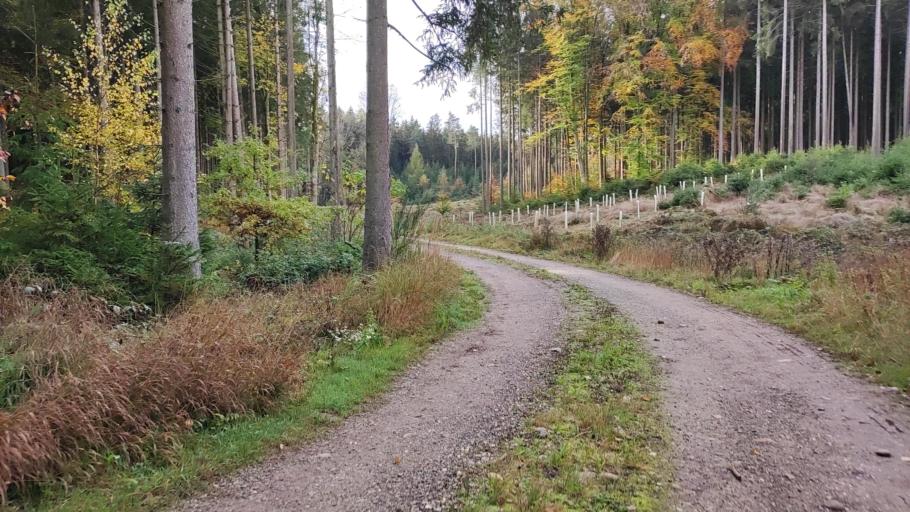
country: DE
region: Bavaria
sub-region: Swabia
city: Ziemetshausen
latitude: 48.3357
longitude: 10.5225
